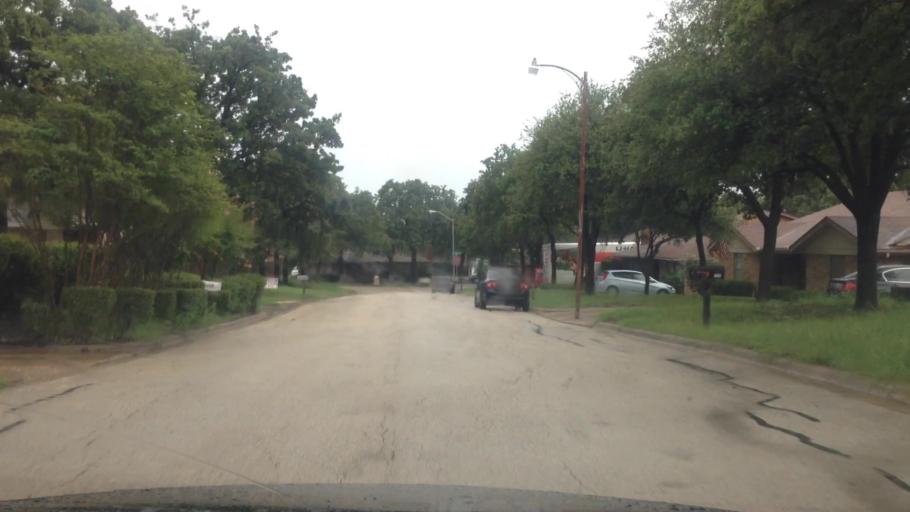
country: US
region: Texas
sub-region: Tarrant County
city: Watauga
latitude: 32.8850
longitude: -97.2291
